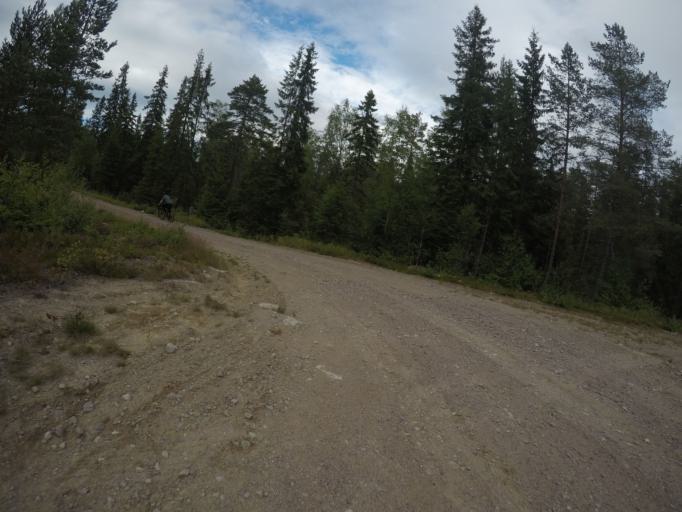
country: SE
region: OErebro
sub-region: Hallefors Kommun
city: Haellefors
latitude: 60.0219
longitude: 14.4731
